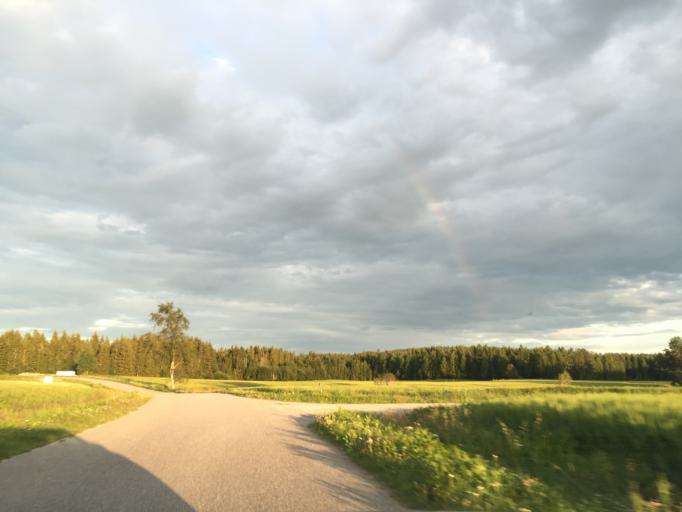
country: NO
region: Akershus
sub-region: Nes
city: Fjellfoten
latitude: 60.0910
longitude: 11.4868
